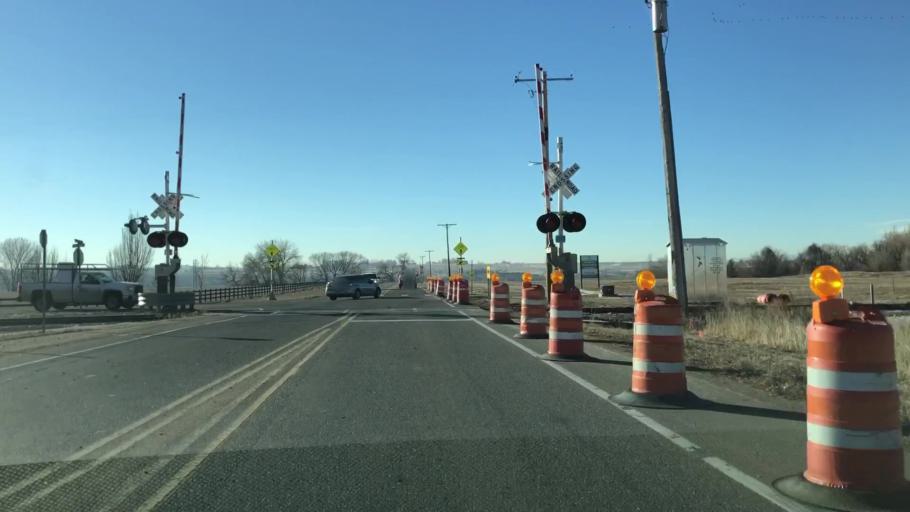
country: US
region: Colorado
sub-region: Larimer County
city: Loveland
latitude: 40.4002
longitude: -105.0212
